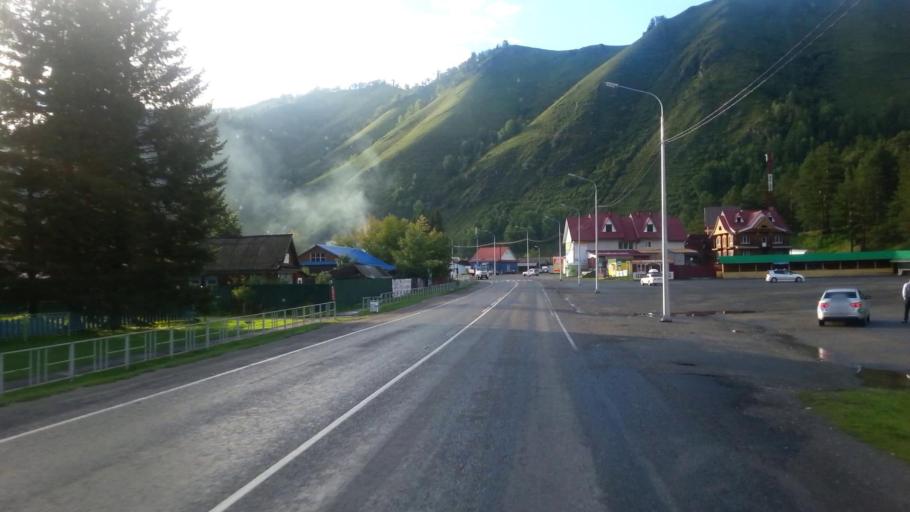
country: RU
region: Altay
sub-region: Mayminskiy Rayon
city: Manzherok
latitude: 51.8324
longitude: 85.7819
